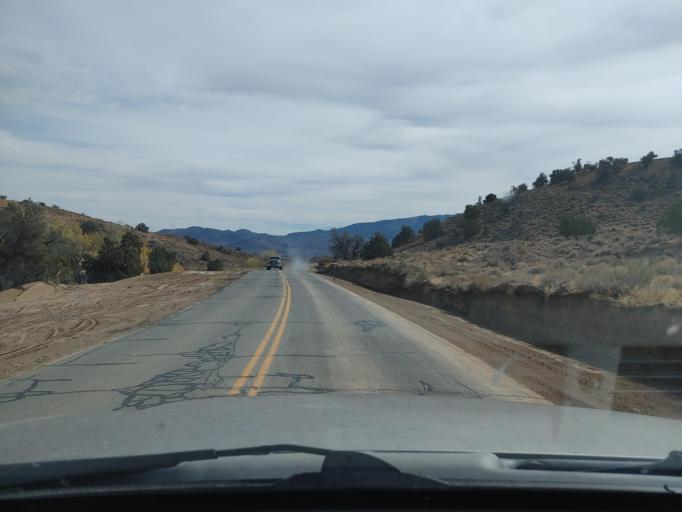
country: US
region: Nevada
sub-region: Storey County
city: Virginia City
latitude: 39.3103
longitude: -119.5749
